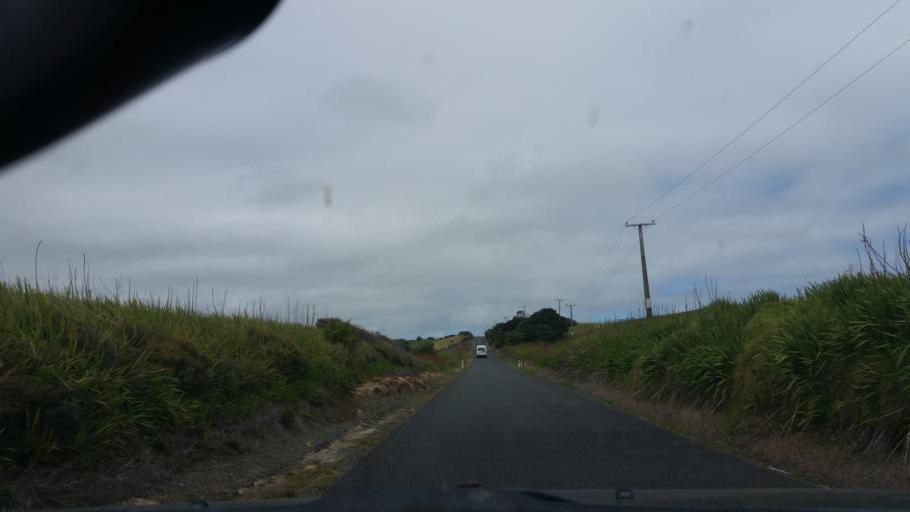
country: NZ
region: Northland
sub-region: Kaipara District
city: Dargaville
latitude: -35.8124
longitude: 173.6392
